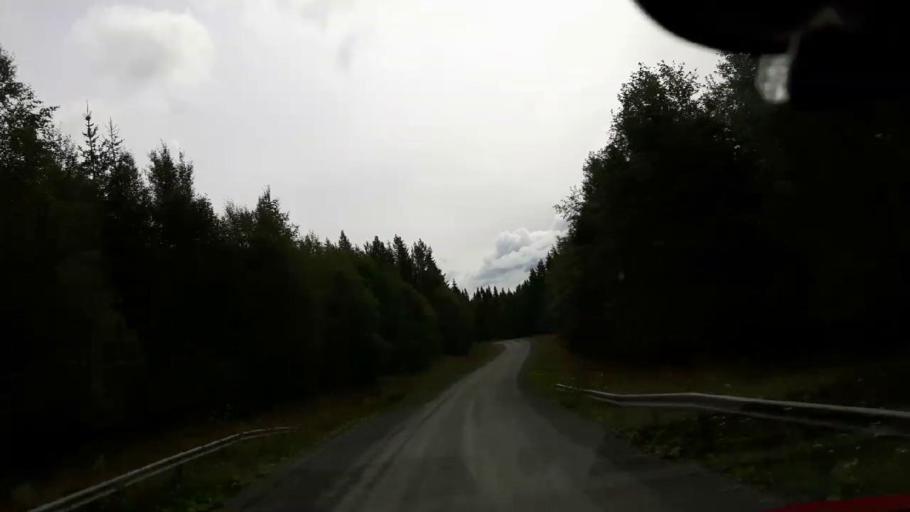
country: SE
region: Jaemtland
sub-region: Krokoms Kommun
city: Valla
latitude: 63.6636
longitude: 13.9677
